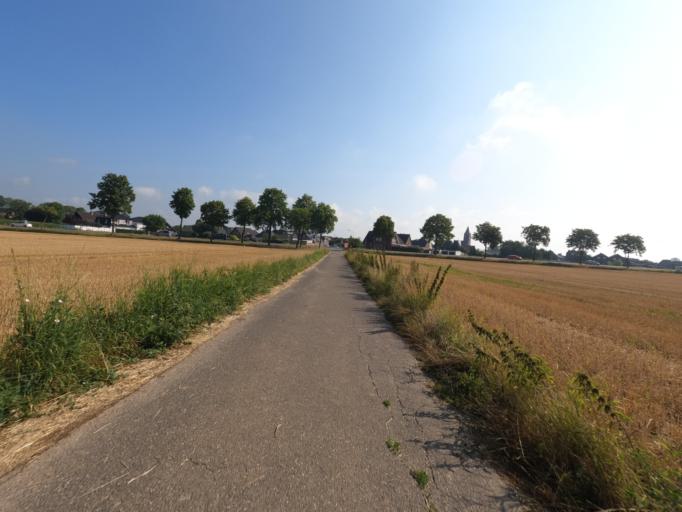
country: DE
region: North Rhine-Westphalia
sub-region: Regierungsbezirk Koln
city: Heinsberg
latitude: 51.0916
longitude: 6.0959
